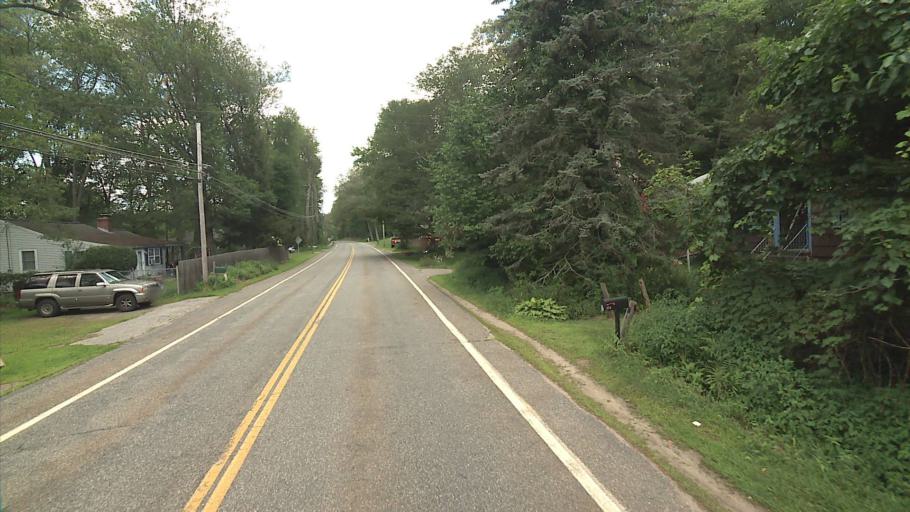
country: US
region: Connecticut
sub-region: Tolland County
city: Stafford
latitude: 41.9357
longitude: -72.1926
